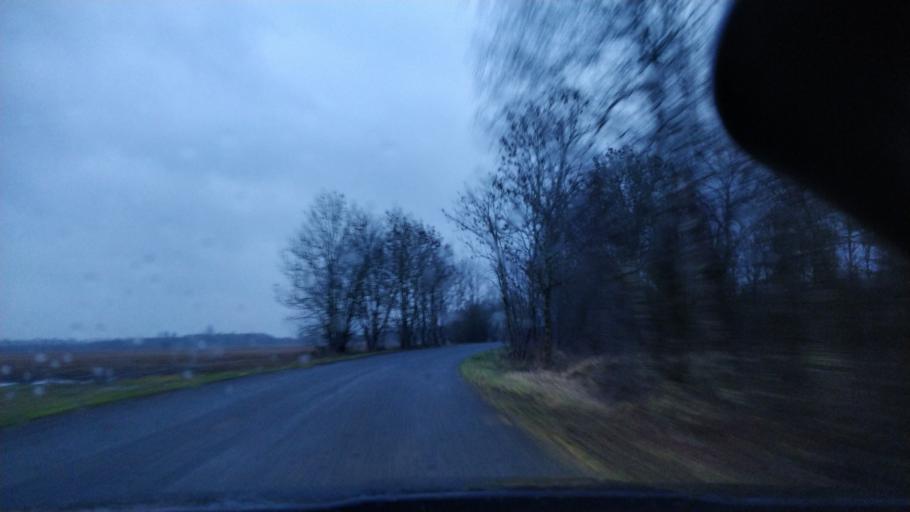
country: EE
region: Laeaene
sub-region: Lihula vald
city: Lihula
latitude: 58.8528
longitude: 24.0160
